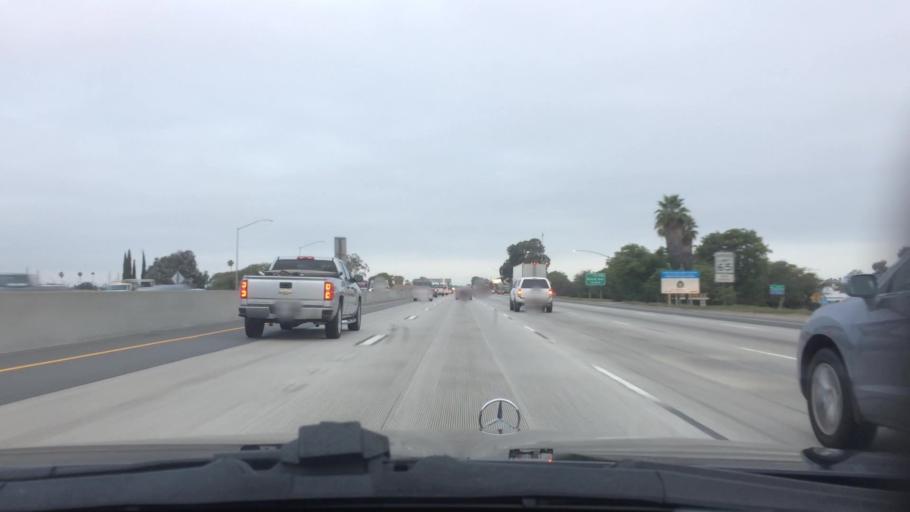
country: US
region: California
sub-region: Orange County
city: Buena Park
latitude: 33.8553
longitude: -117.9958
